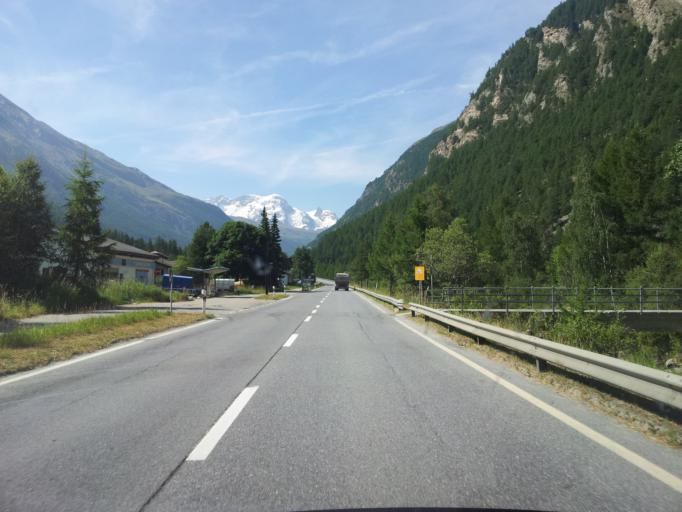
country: CH
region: Valais
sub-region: Visp District
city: Zermatt
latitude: 46.0976
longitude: 7.7802
